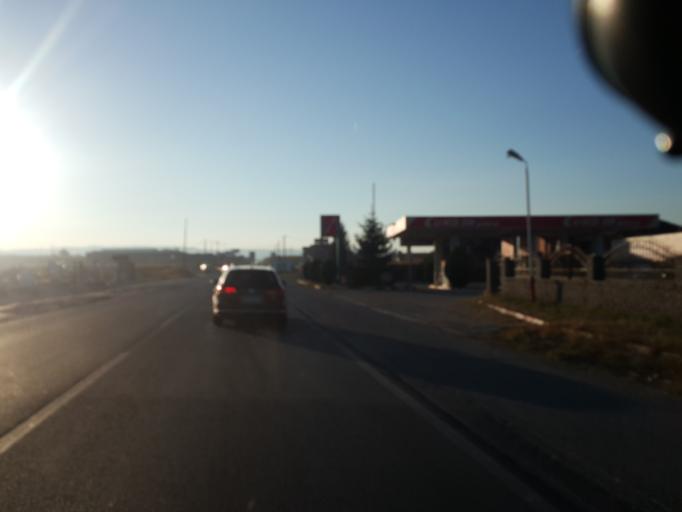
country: XK
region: Prizren
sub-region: Komuna e Malisheves
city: Llazice
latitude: 42.5765
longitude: 20.7063
